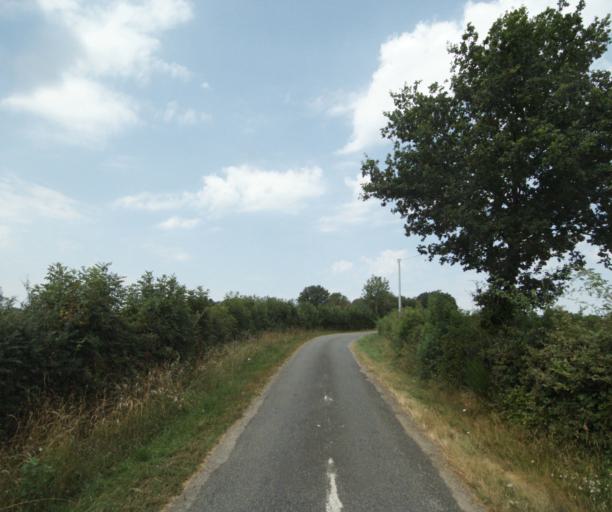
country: FR
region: Bourgogne
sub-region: Departement de Saone-et-Loire
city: Gueugnon
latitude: 46.5863
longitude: 4.0348
